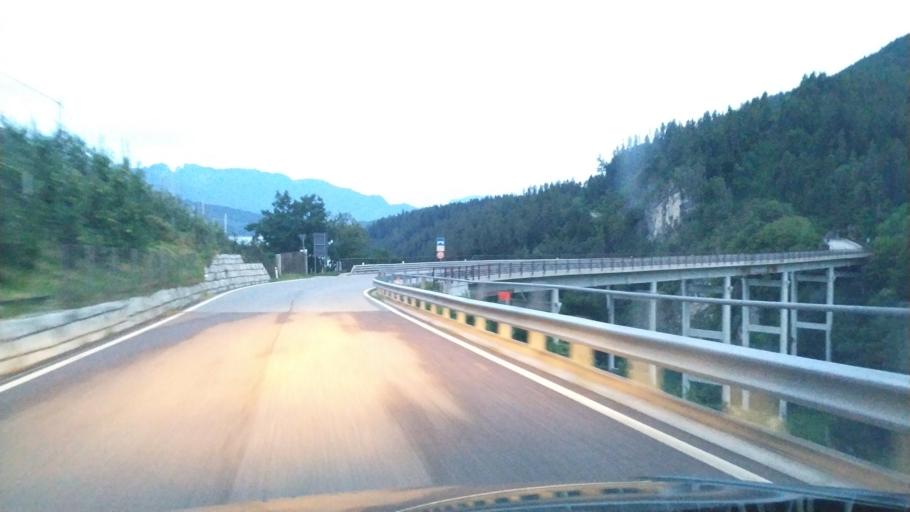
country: IT
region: Trentino-Alto Adige
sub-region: Provincia di Trento
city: Cagno
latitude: 46.3900
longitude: 11.0383
